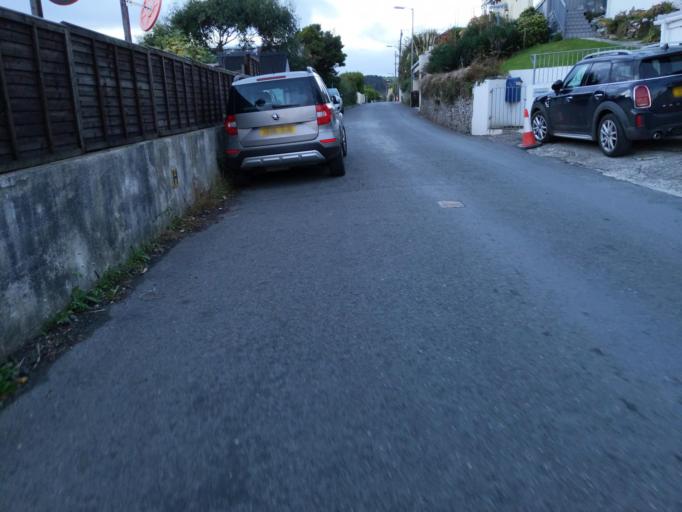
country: GB
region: England
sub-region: Cornwall
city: Looe
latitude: 50.3626
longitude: -4.3761
